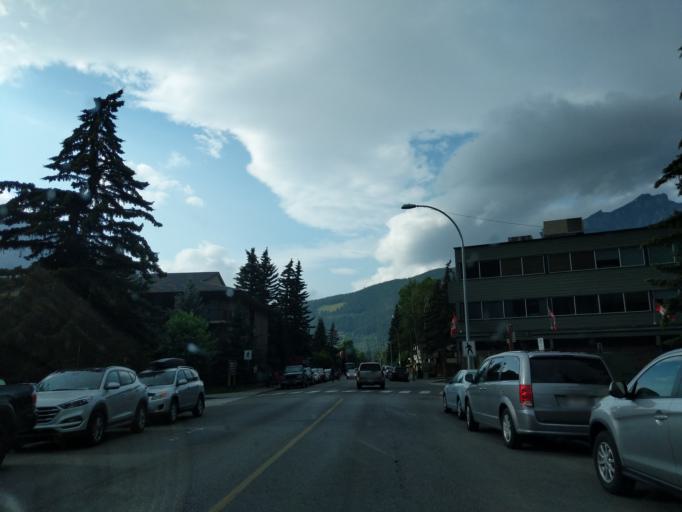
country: CA
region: Alberta
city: Banff
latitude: 51.1763
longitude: -115.5730
